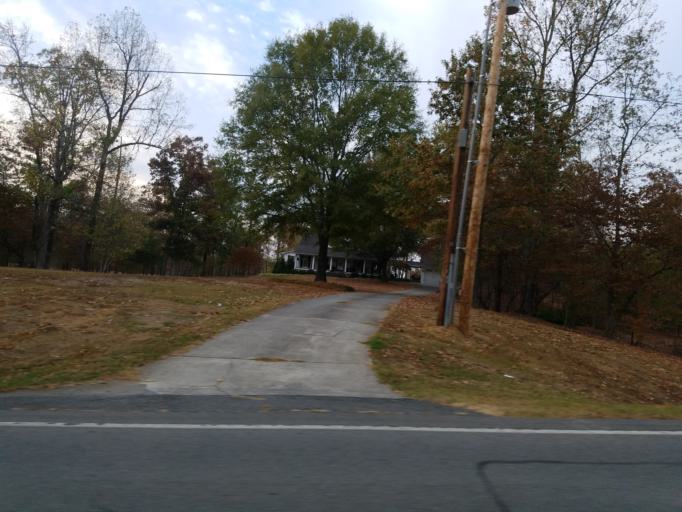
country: US
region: Georgia
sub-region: Gordon County
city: Calhoun
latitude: 34.5958
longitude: -84.8929
